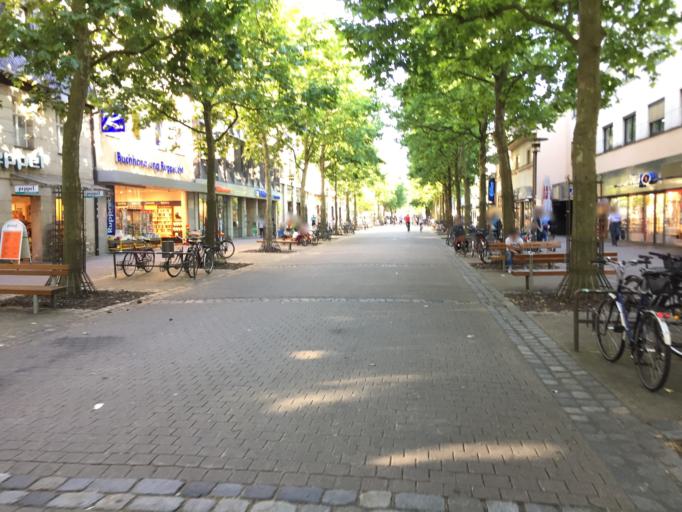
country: DE
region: Bavaria
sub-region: Regierungsbezirk Mittelfranken
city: Erlangen
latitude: 49.5936
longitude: 11.0053
